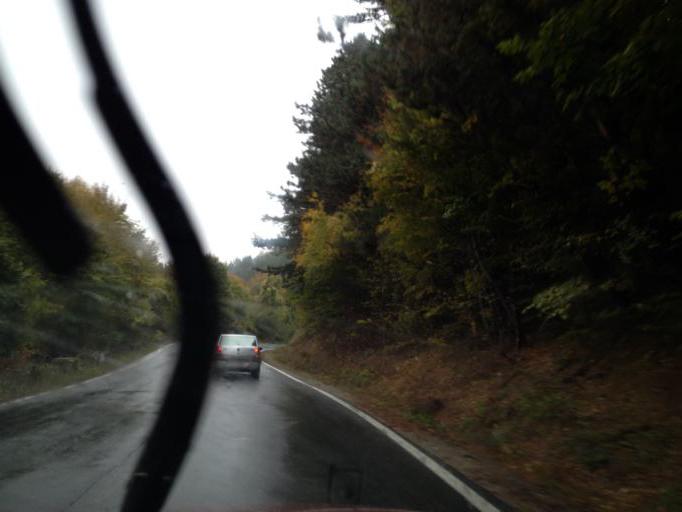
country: RO
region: Arges
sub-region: Comuna Dragoslavele
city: Dragoslavele
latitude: 45.3032
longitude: 25.1543
